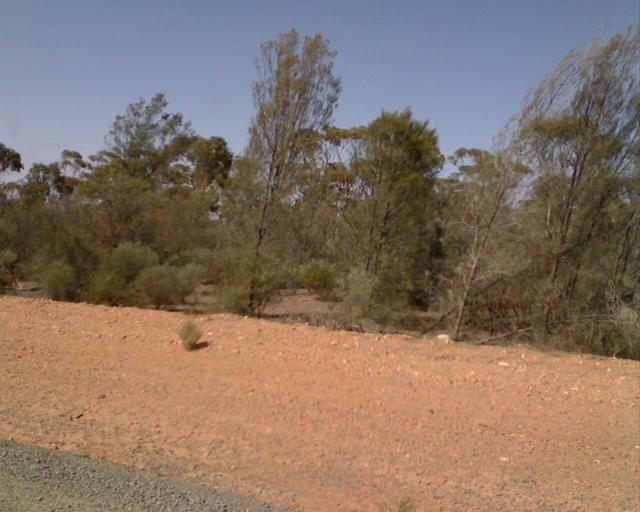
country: AU
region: Western Australia
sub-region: Kalgoorlie/Boulder
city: Boulder
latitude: -30.8357
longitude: 121.3836
